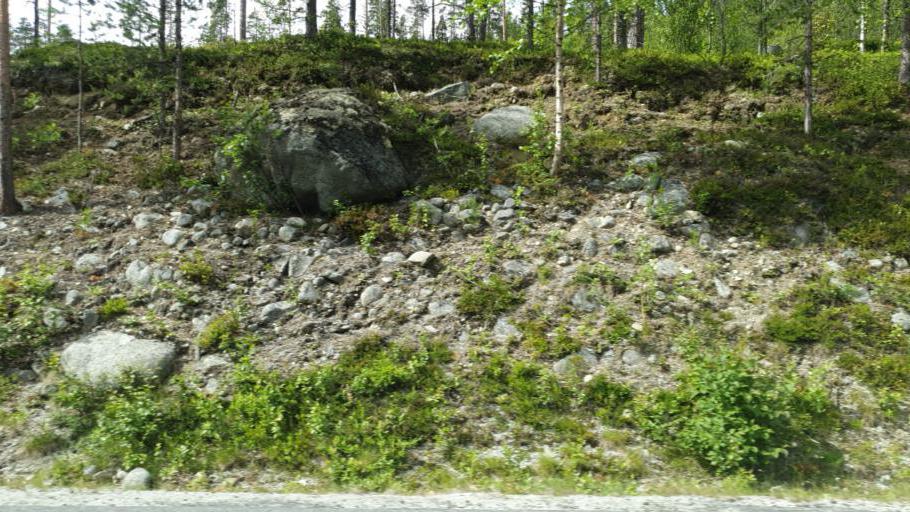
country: NO
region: Oppland
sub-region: Vaga
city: Vagamo
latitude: 61.7389
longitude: 9.0913
